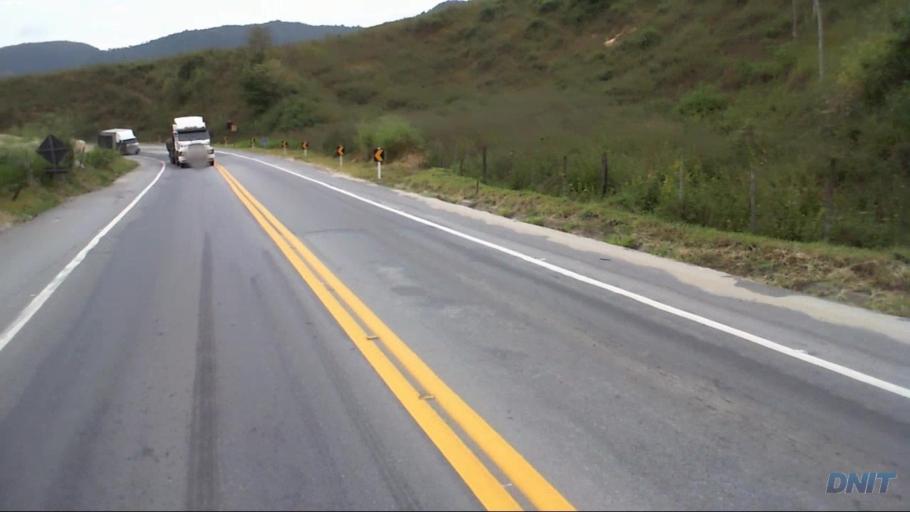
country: BR
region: Minas Gerais
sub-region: Timoteo
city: Timoteo
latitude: -19.6185
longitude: -42.7860
